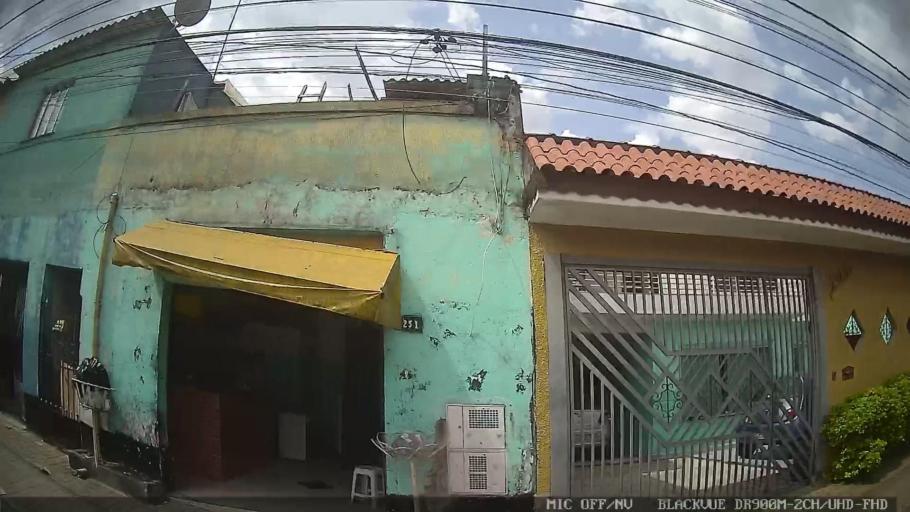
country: BR
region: Sao Paulo
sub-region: Poa
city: Poa
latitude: -23.5316
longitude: -46.3362
